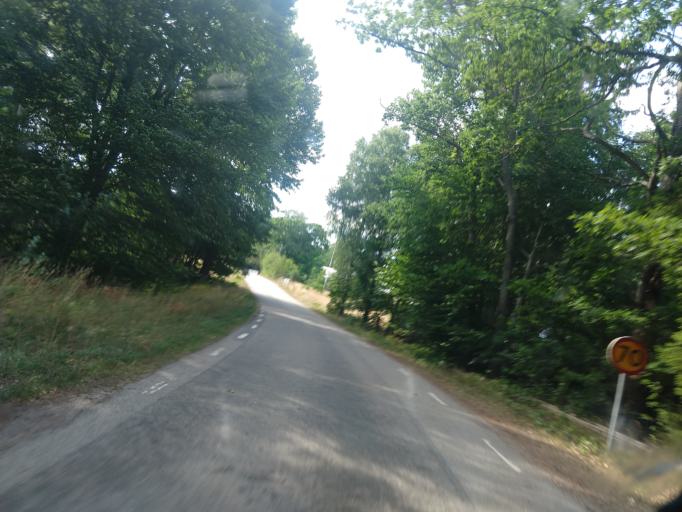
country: SE
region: Blekinge
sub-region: Karlskrona Kommun
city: Nattraby
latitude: 56.2570
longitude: 15.5230
